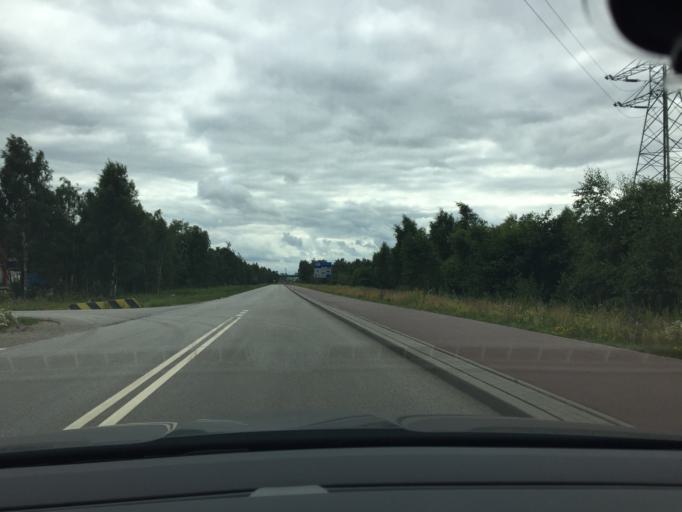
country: PL
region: Pomeranian Voivodeship
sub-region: Gdansk
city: Gdansk
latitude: 54.3846
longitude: 18.6837
